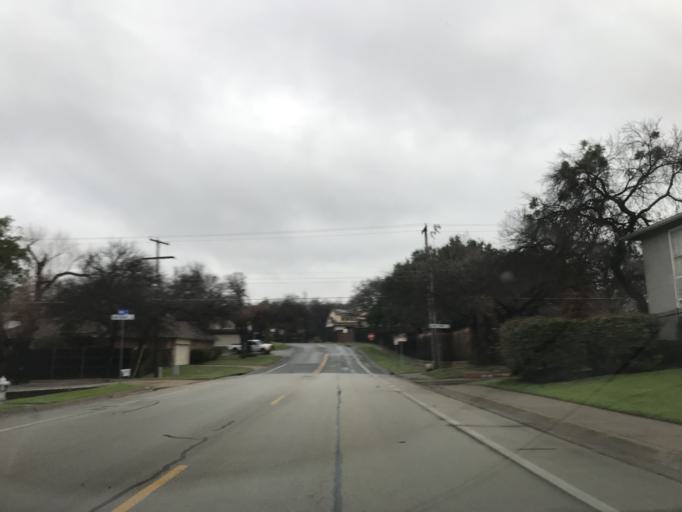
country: US
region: Texas
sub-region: Tarrant County
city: Arlington
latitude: 32.7716
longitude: -97.1051
